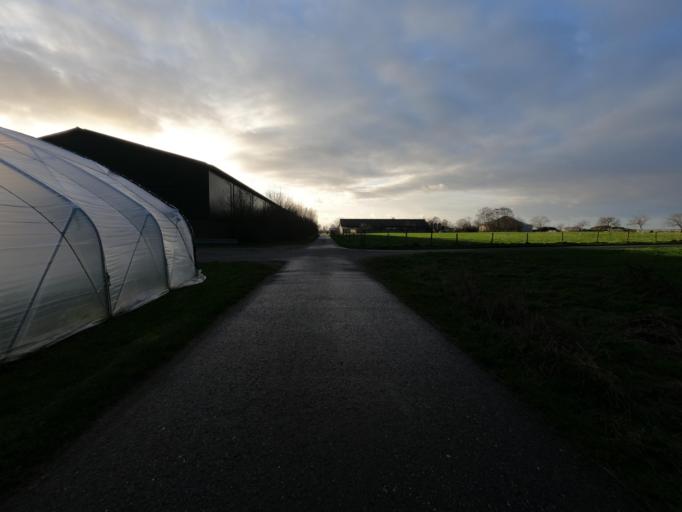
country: DE
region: North Rhine-Westphalia
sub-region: Regierungsbezirk Koln
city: Heinsberg
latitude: 51.0638
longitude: 6.0686
